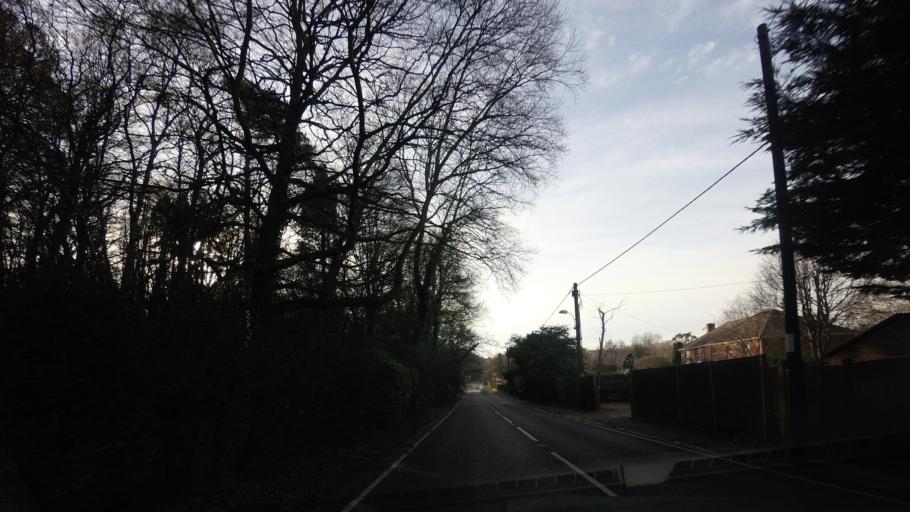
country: GB
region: England
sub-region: East Sussex
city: Battle
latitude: 50.8912
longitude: 0.4408
